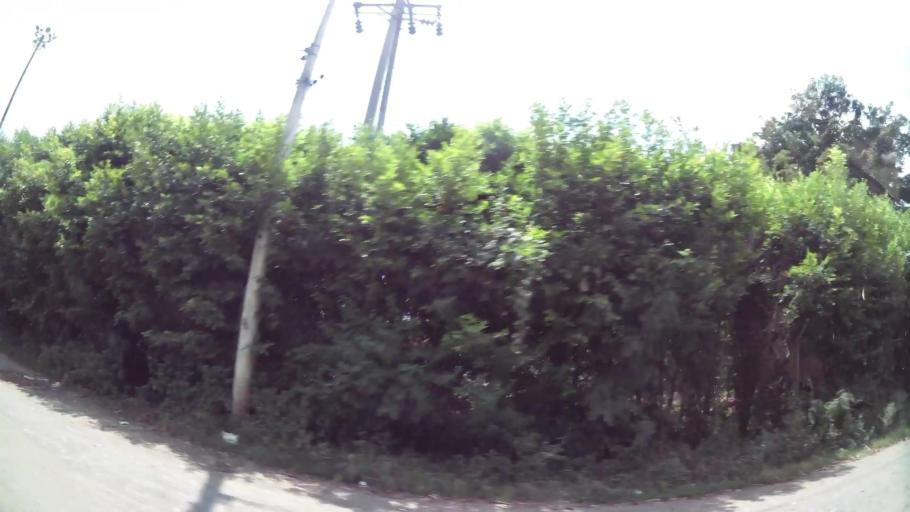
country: CO
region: Valle del Cauca
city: Cali
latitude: 3.4721
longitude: -76.4798
